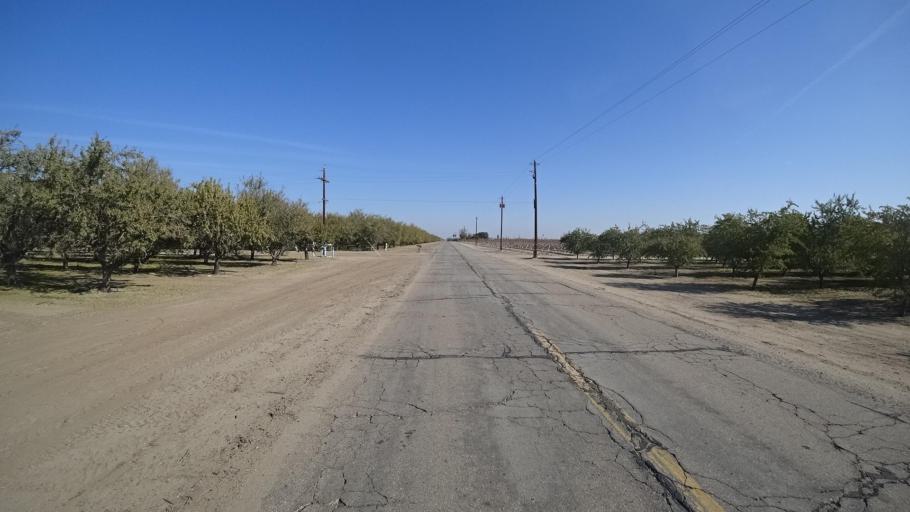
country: US
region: California
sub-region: Kern County
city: Wasco
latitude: 35.6669
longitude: -119.3711
